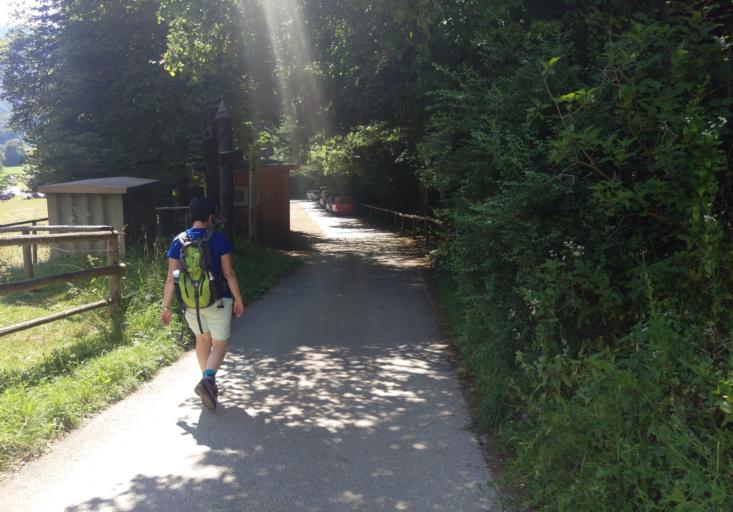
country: AT
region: Styria
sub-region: Politischer Bezirk Graz-Umgebung
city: Rothelstein
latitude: 47.3361
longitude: 15.3745
